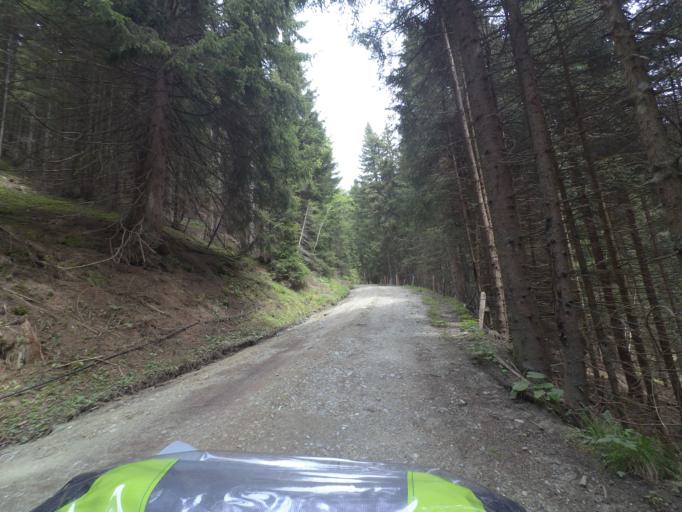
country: AT
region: Salzburg
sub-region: Politischer Bezirk Sankt Johann im Pongau
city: Dorfgastein
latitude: 47.2589
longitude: 13.1242
